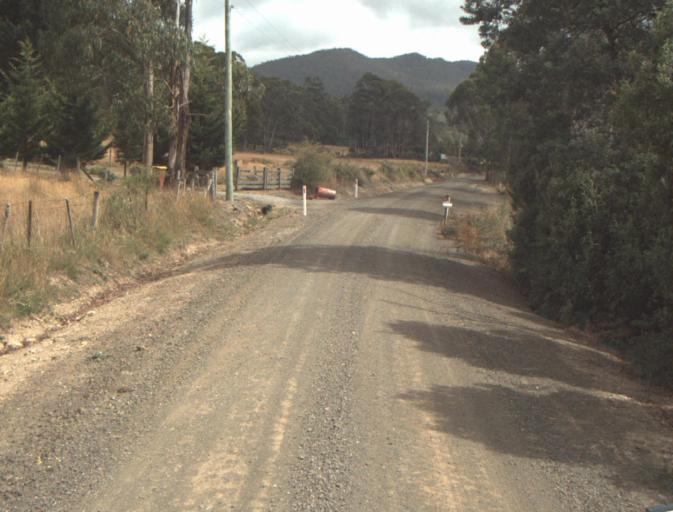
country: AU
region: Tasmania
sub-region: Northern Midlands
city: Evandale
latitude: -41.4603
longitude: 147.4480
